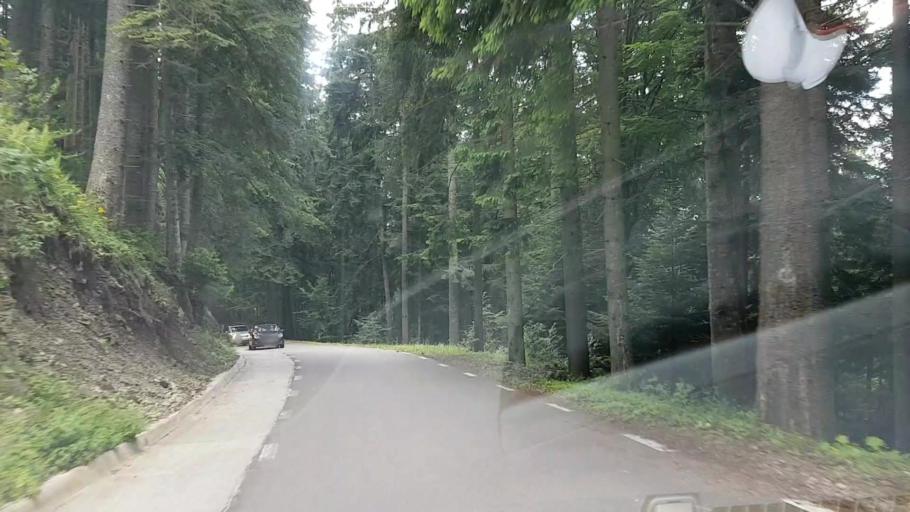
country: RO
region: Suceava
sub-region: Municipiul Campulung Moldovenesc
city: Campulung Moldovenesc
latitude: 47.4356
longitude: 25.5683
